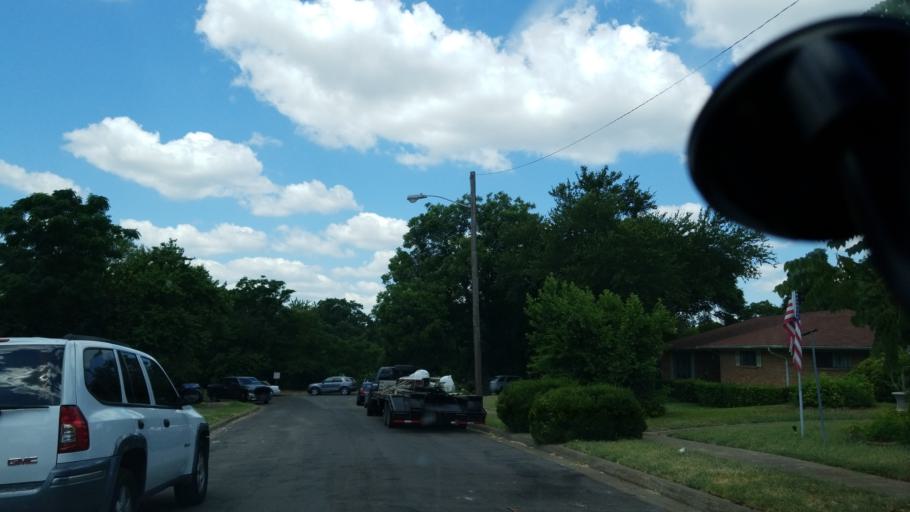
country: US
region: Texas
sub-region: Dallas County
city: Cockrell Hill
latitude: 32.7030
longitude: -96.8426
